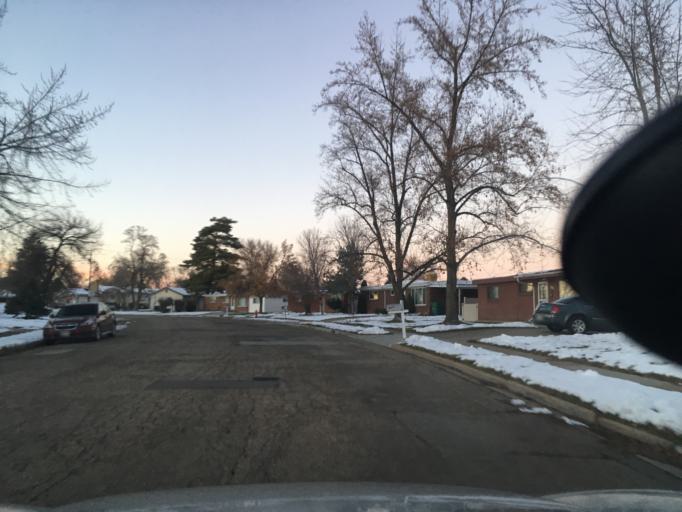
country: US
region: Utah
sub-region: Davis County
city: Layton
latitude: 41.0649
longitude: -111.9650
